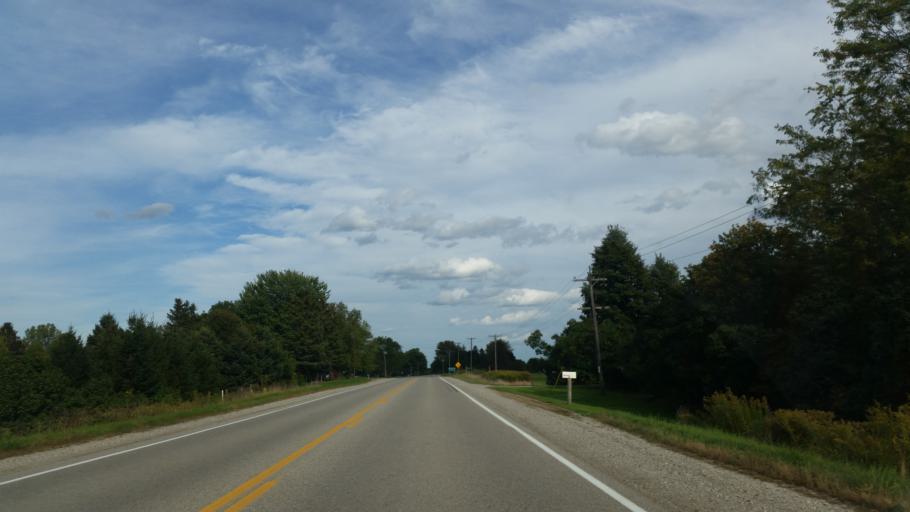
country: CA
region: Ontario
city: Delaware
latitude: 42.8822
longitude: -81.4598
